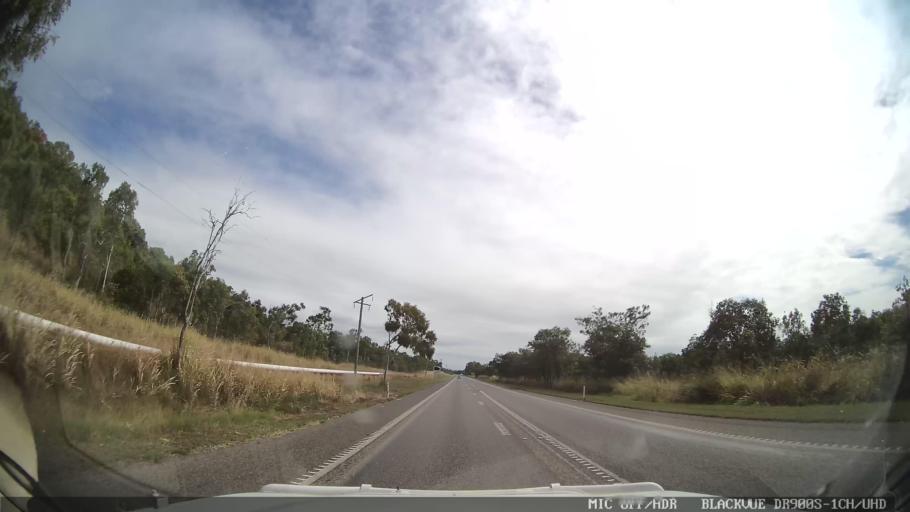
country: AU
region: Queensland
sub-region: Hinchinbrook
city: Ingham
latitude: -19.0072
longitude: 146.3611
